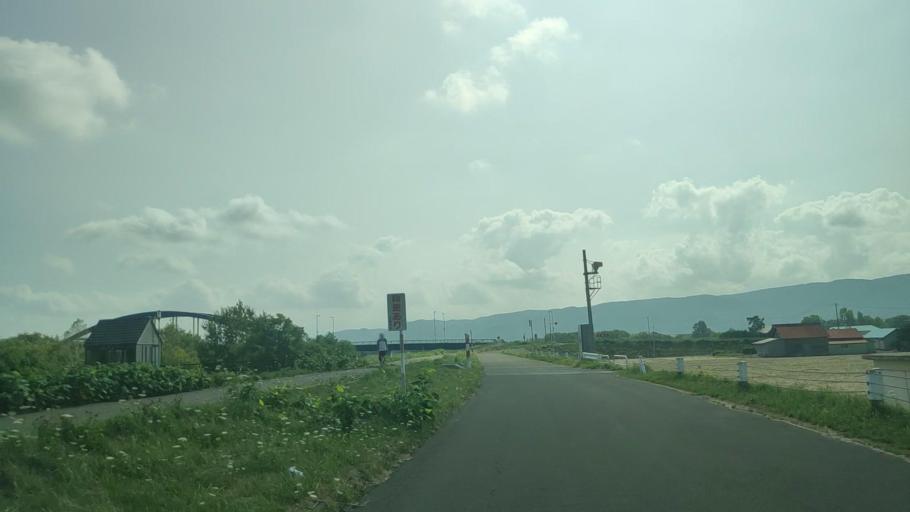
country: JP
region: Hokkaido
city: Shimo-furano
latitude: 43.3371
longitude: 142.3817
